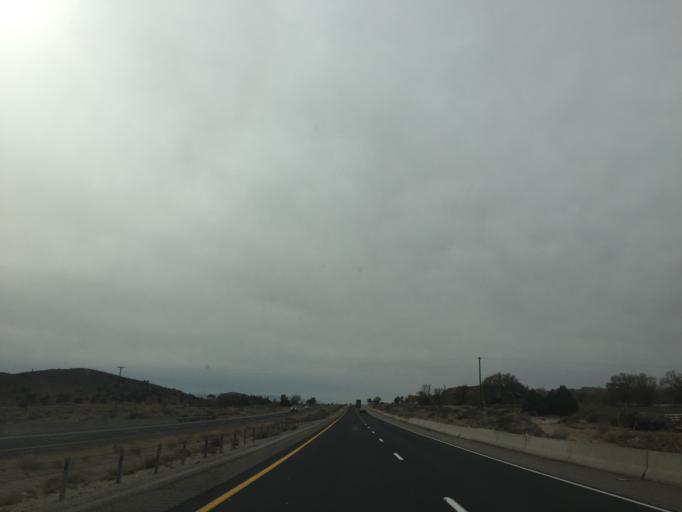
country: US
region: Utah
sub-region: Washington County
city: Toquerville
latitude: 37.2507
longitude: -113.3432
